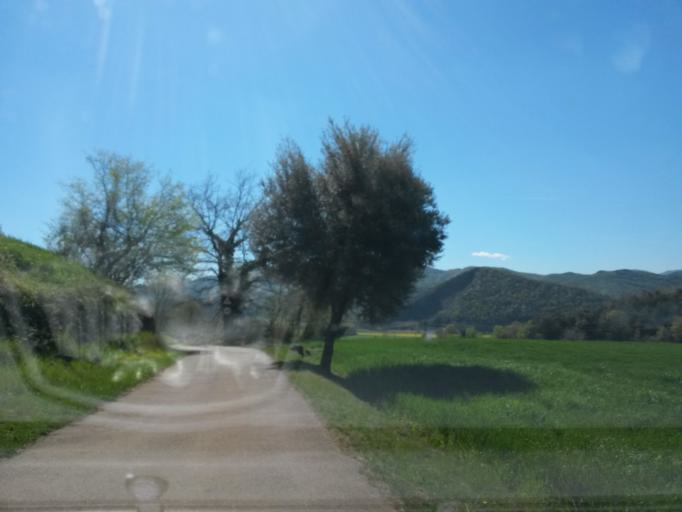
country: ES
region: Catalonia
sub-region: Provincia de Girona
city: Sant Cristofol de les Fonts
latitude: 42.1701
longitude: 2.5330
